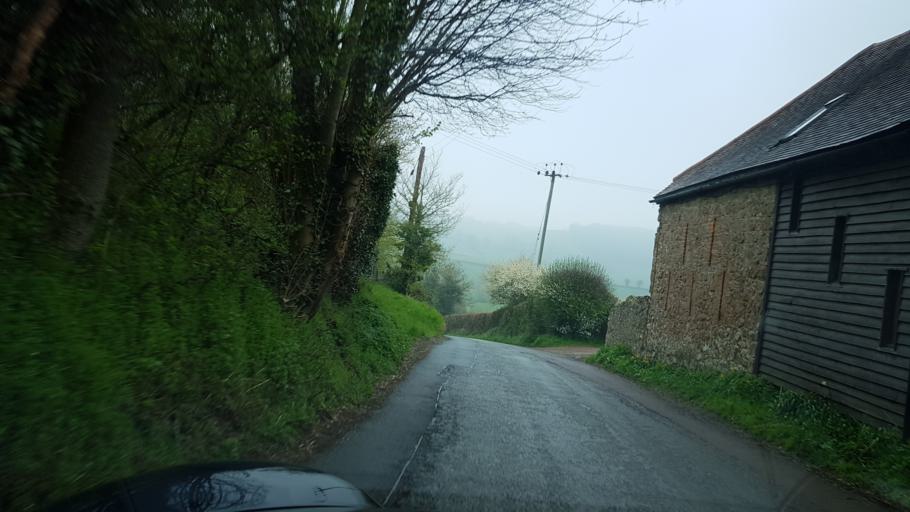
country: GB
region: England
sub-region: Herefordshire
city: Brockhampton
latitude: 52.0179
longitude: -2.5660
